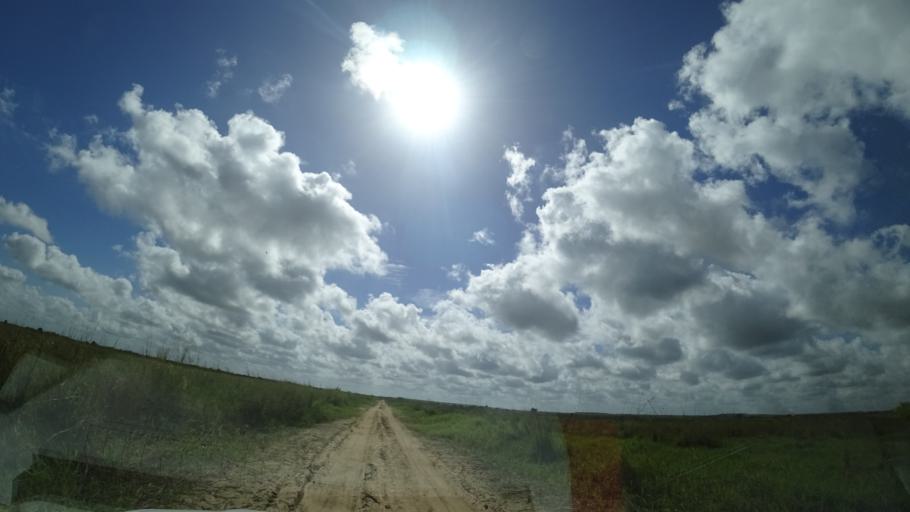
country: MZ
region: Sofala
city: Dondo
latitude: -19.3968
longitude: 34.5715
